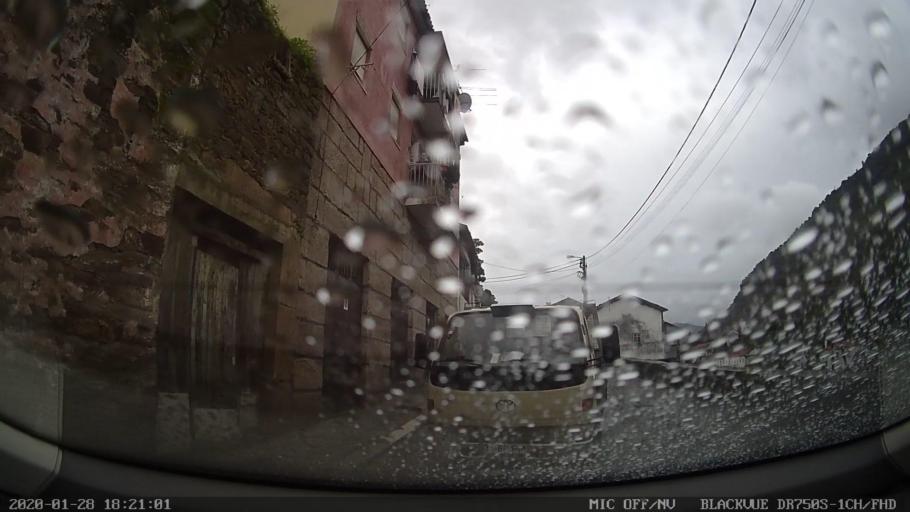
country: PT
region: Vila Real
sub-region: Sabrosa
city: Vilela
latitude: 41.1965
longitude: -7.5542
